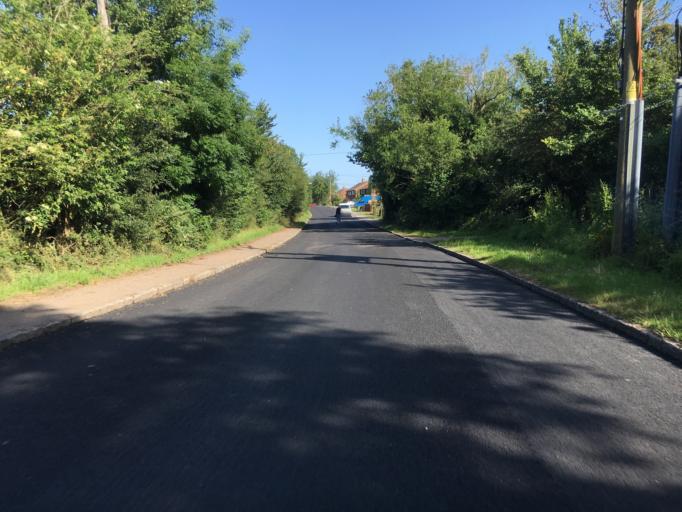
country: GB
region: England
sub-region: Buckinghamshire
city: Steeple Claydon
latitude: 51.9307
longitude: -1.0347
